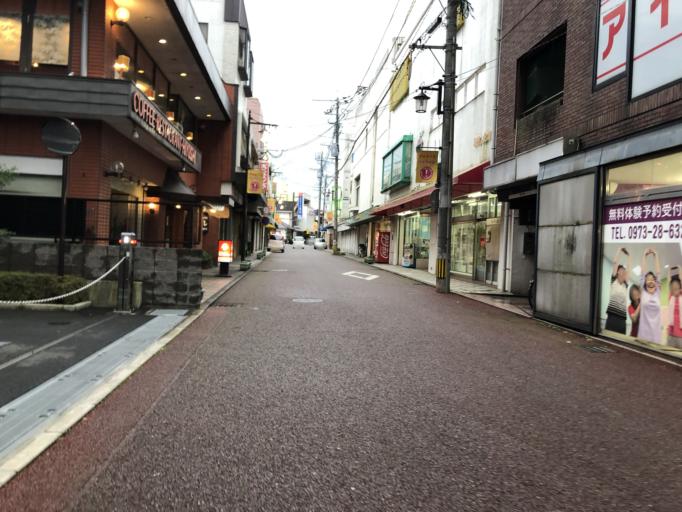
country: JP
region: Oita
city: Hita
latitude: 33.3186
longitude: 130.9367
